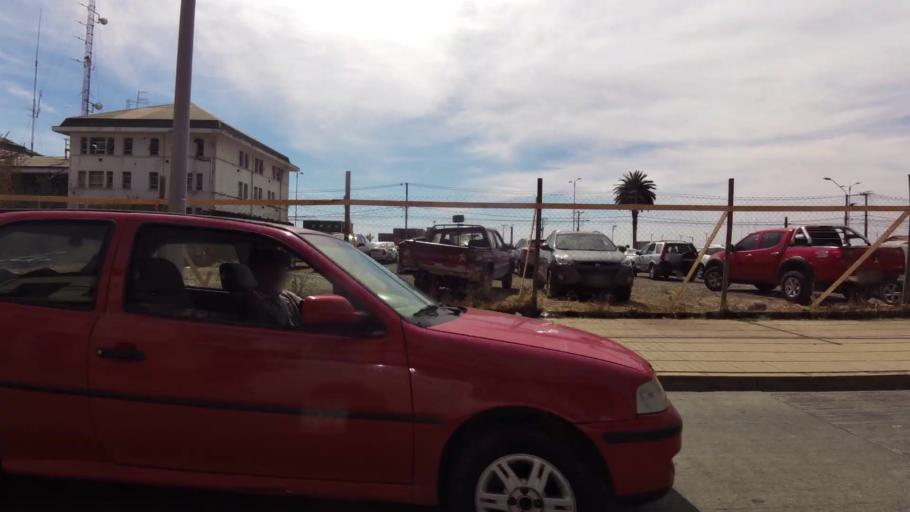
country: CL
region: Biobio
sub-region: Provincia de Concepcion
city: Talcahuano
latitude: -36.7165
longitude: -73.1097
